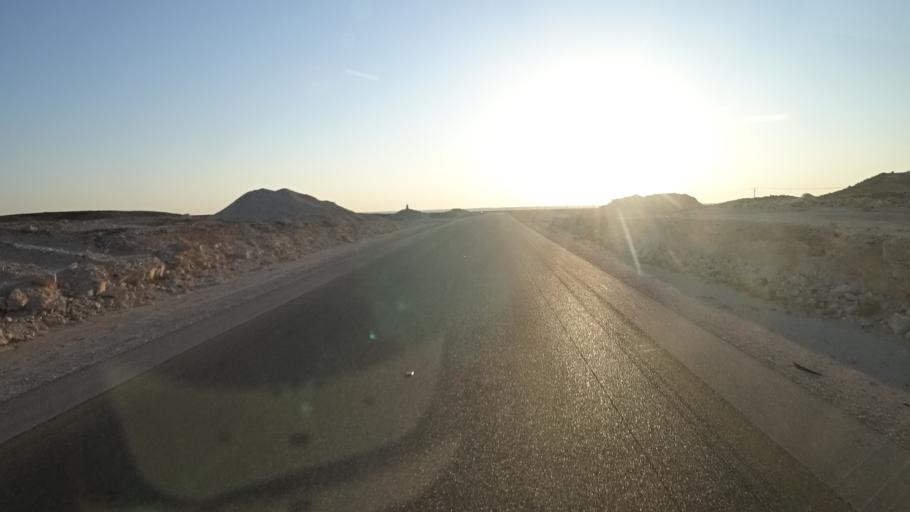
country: OM
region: Zufar
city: Salalah
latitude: 17.5389
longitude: 53.4131
